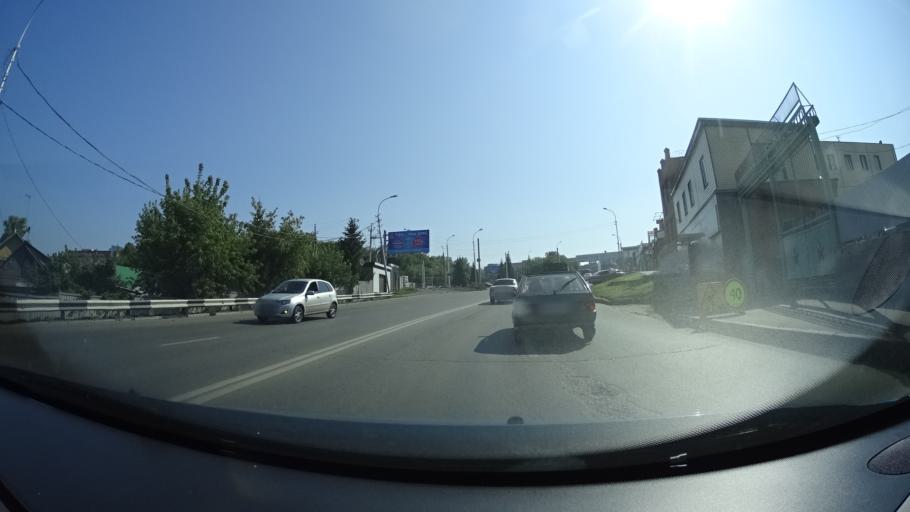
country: RU
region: Bashkortostan
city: Ufa
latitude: 54.7484
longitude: 55.9726
